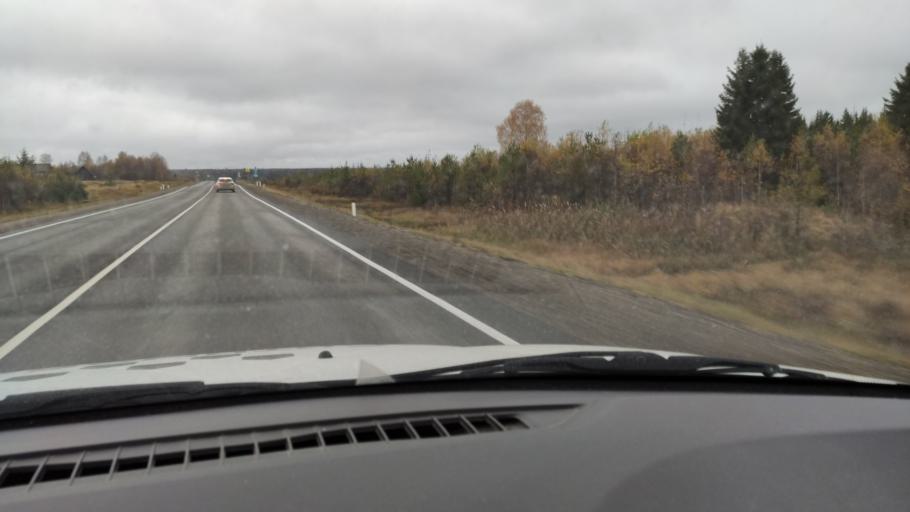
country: RU
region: Kirov
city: Chernaya Kholunitsa
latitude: 58.8581
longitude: 51.7146
